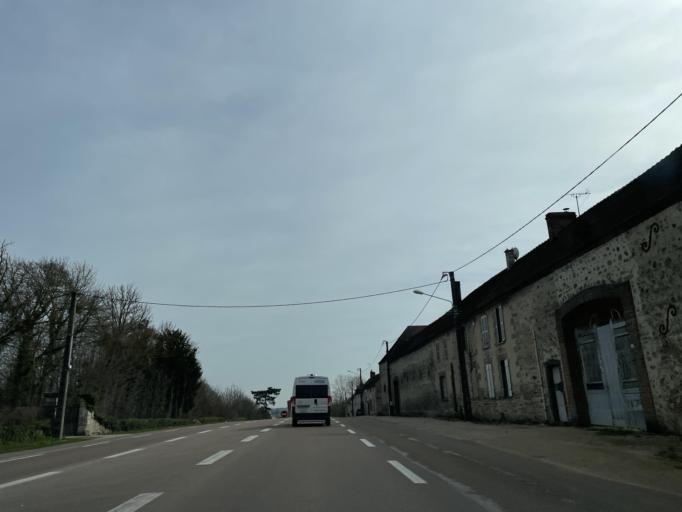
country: FR
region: Champagne-Ardenne
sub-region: Departement de l'Aube
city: Villenauxe-la-Grande
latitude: 48.5093
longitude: 3.5968
